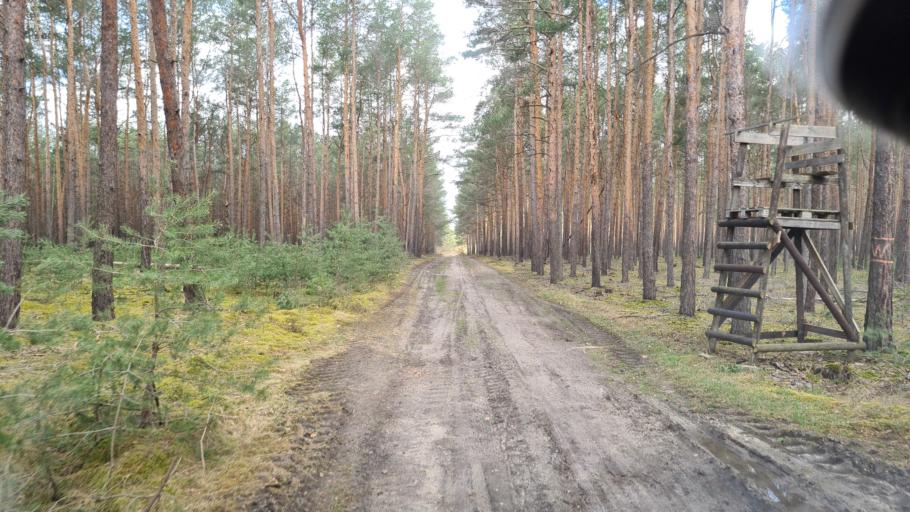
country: DE
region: Brandenburg
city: Trobitz
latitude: 51.6553
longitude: 13.4528
